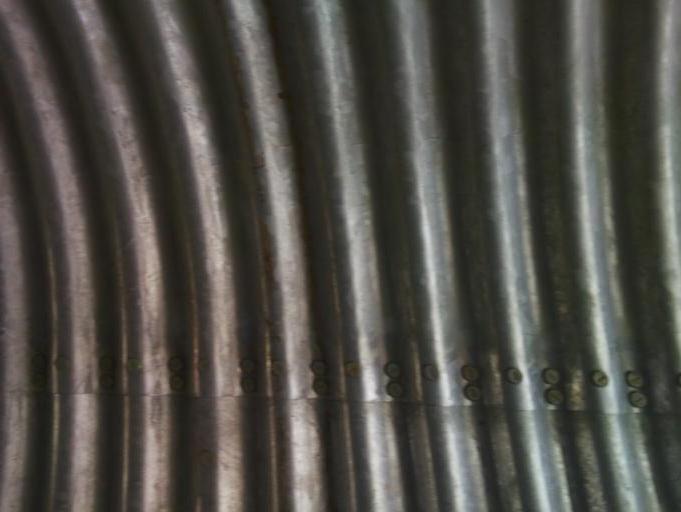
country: CH
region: Zurich
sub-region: Bezirk Andelfingen
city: Grossandelfingen
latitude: 47.5893
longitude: 8.6681
